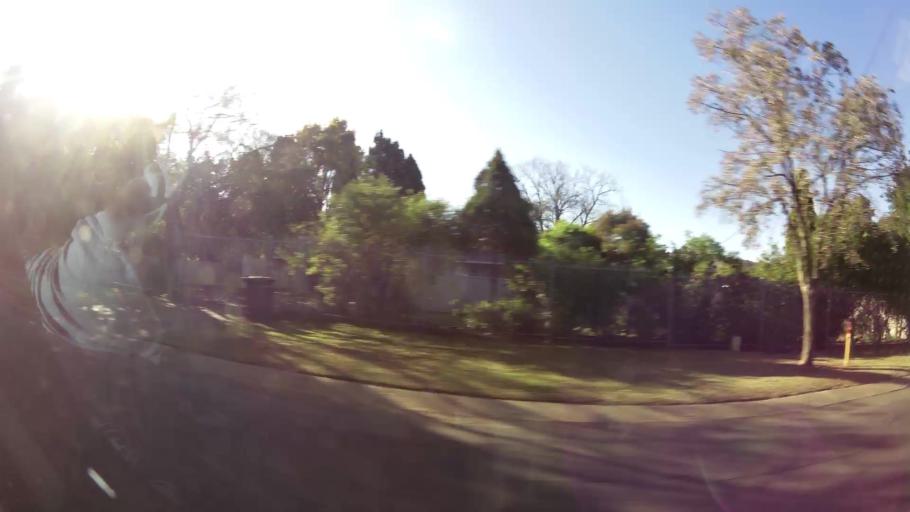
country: ZA
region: Gauteng
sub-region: City of Tshwane Metropolitan Municipality
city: Pretoria
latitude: -25.7020
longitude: 28.2640
